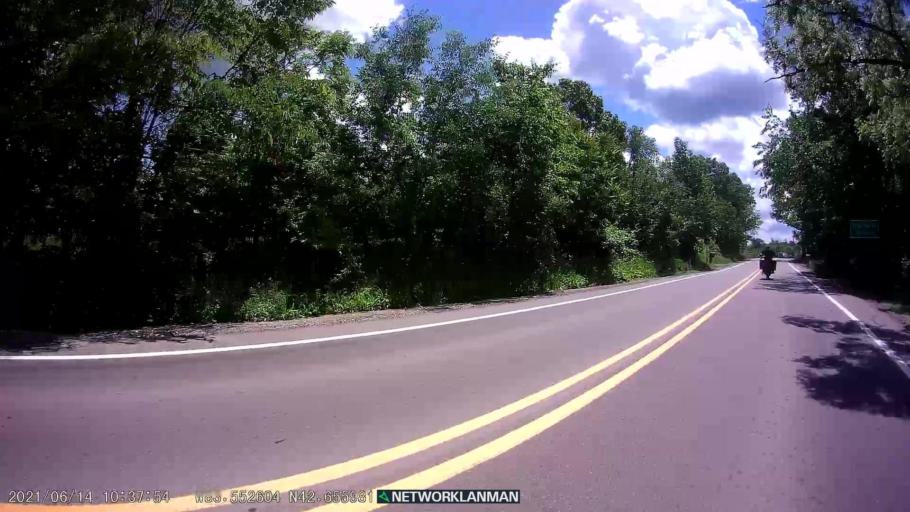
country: US
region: Michigan
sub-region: Oakland County
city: Milford
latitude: 42.6560
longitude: -83.5526
